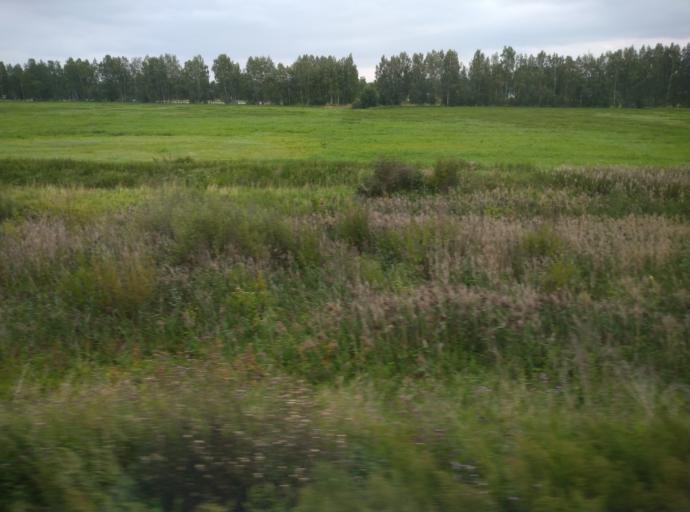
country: RU
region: Kostroma
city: Nerekhta
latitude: 57.4874
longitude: 40.6011
